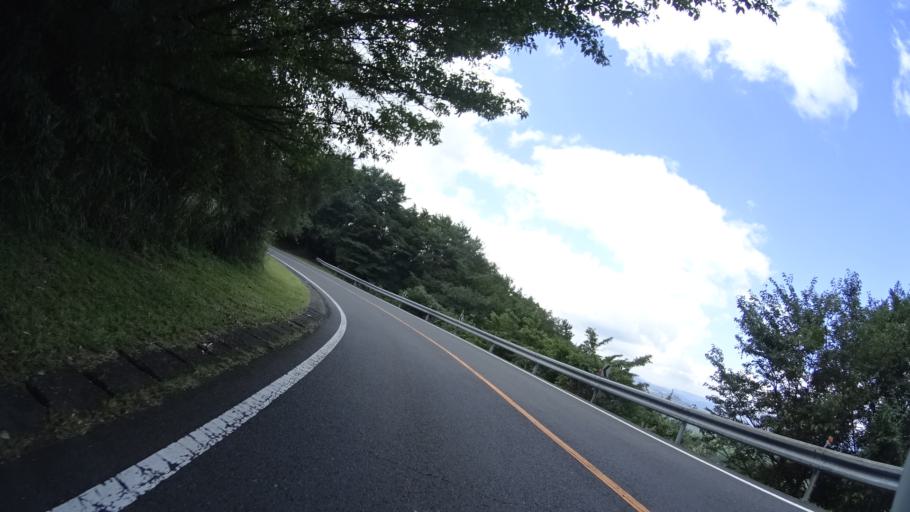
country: JP
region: Oita
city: Tsukawaki
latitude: 33.2447
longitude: 131.2840
